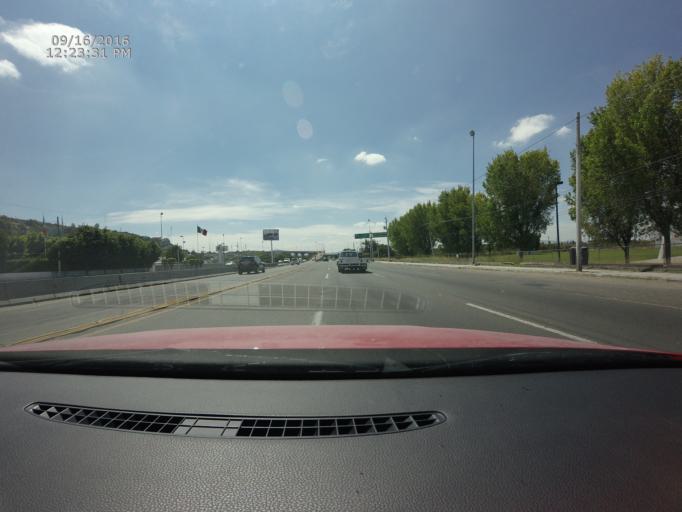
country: MX
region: Queretaro
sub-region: Queretaro
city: Sergio Villasenor
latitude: 20.6261
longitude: -100.4244
